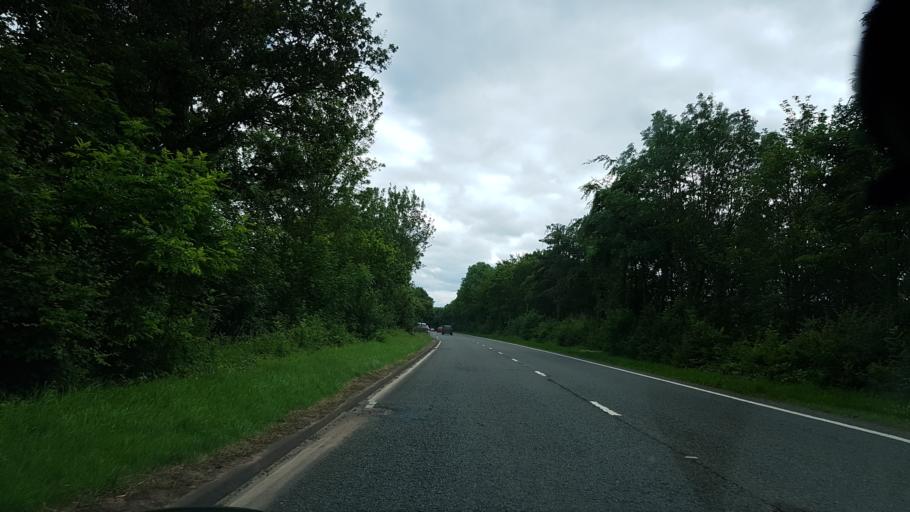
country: GB
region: Wales
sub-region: Monmouthshire
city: Abergavenny
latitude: 51.8179
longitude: -3.0082
